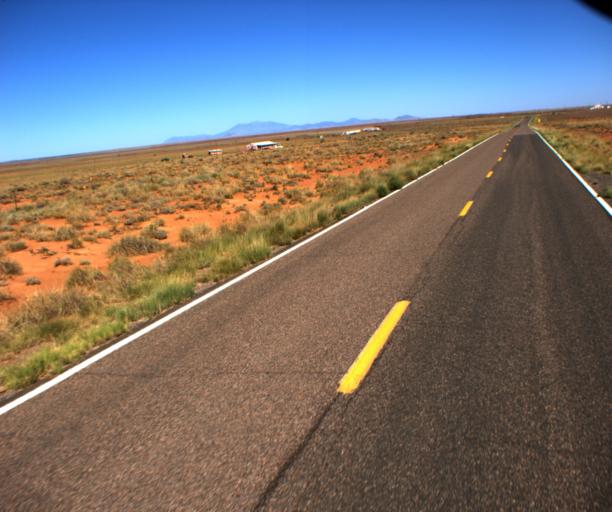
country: US
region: Arizona
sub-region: Coconino County
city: LeChee
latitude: 35.1323
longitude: -110.8819
